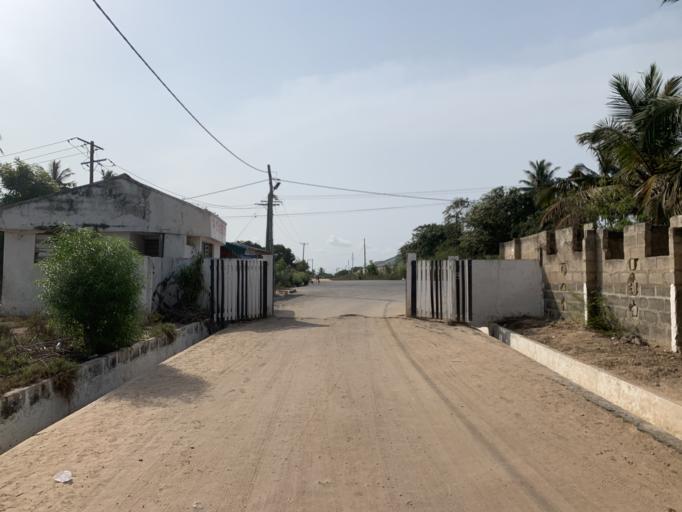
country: GH
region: Central
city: Winneba
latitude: 5.3320
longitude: -0.6275
